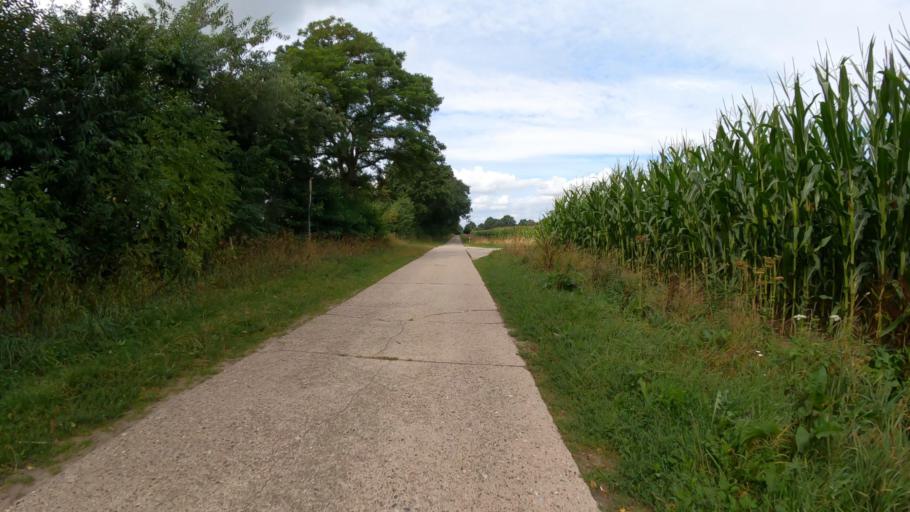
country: DE
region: Lower Saxony
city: Neu Wulmstorf
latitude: 53.4318
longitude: 9.8103
